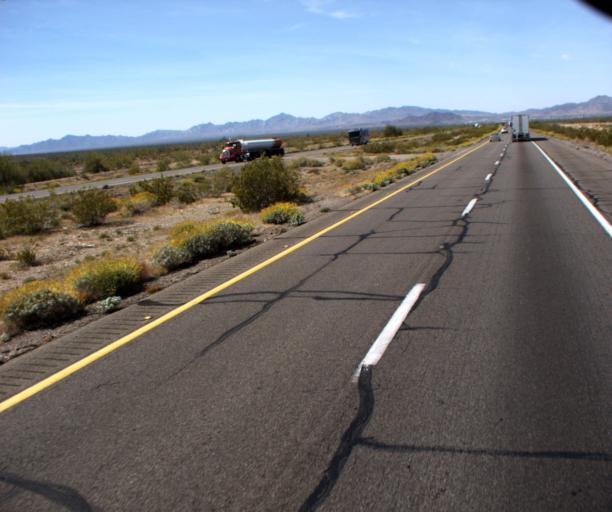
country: US
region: Arizona
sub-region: La Paz County
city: Quartzsite
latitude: 33.6782
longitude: -114.1110
